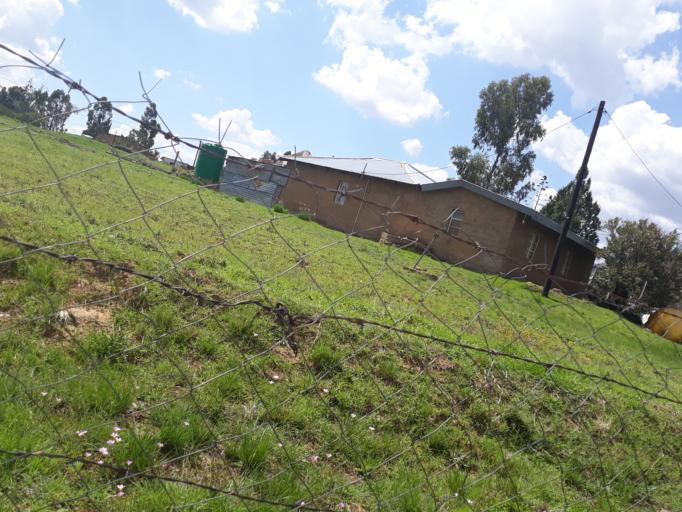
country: LS
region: Quthing
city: Quthing
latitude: -30.3416
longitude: 27.5292
